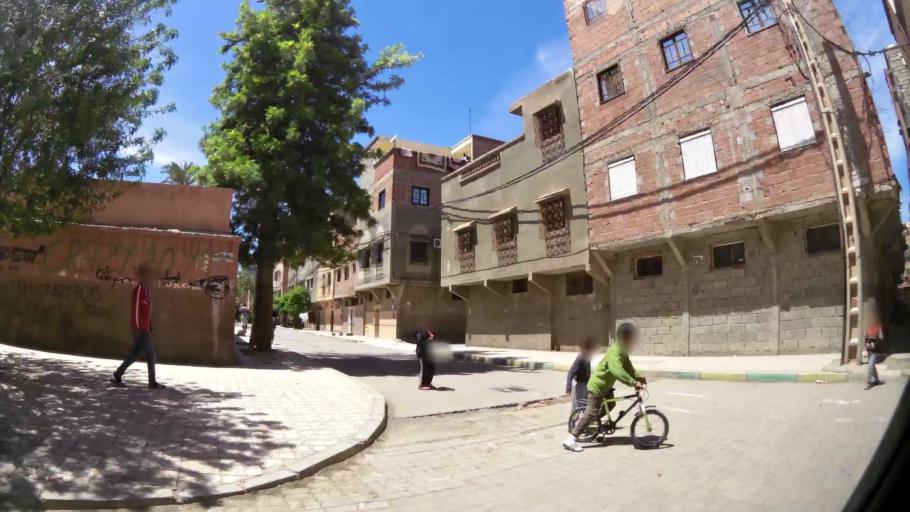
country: MA
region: Marrakech-Tensift-Al Haouz
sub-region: Marrakech
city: Marrakesh
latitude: 31.6579
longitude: -7.9941
